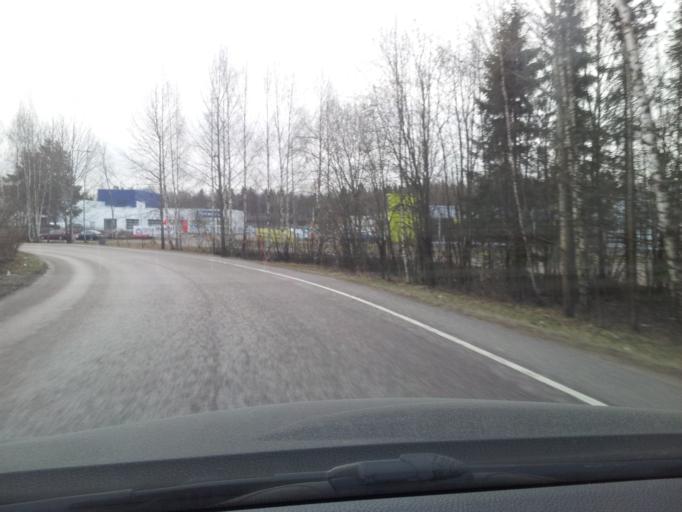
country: FI
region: Uusimaa
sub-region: Helsinki
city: Teekkarikylae
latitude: 60.2330
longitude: 24.8599
